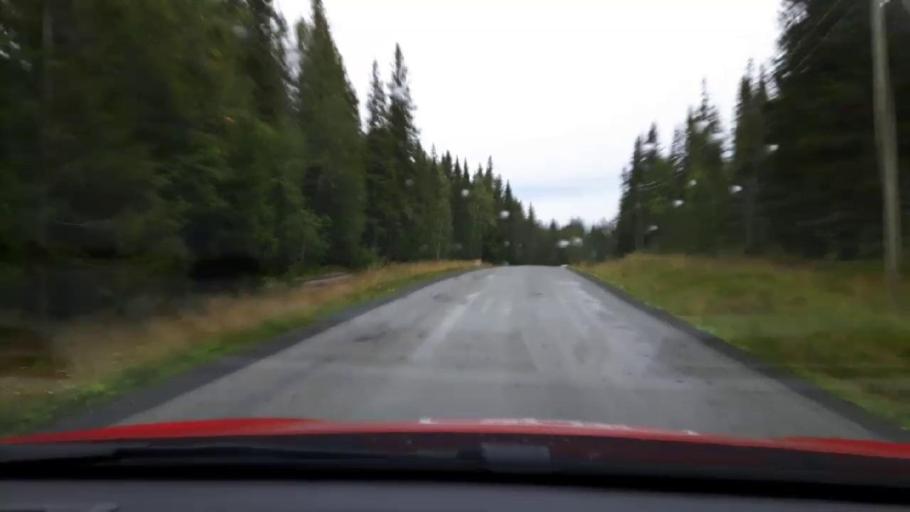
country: SE
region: Jaemtland
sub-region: Are Kommun
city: Are
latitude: 63.4633
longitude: 13.1914
